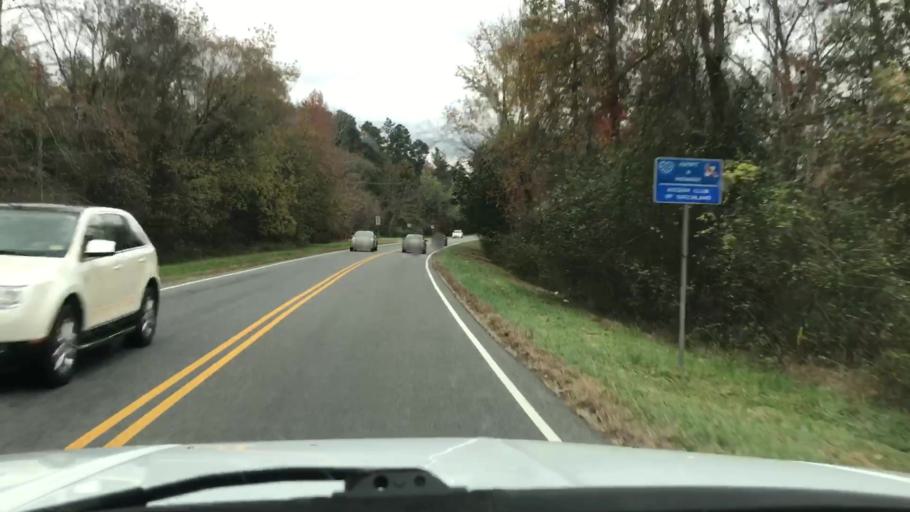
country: US
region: Virginia
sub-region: Henrico County
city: Short Pump
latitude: 37.6162
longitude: -77.7537
